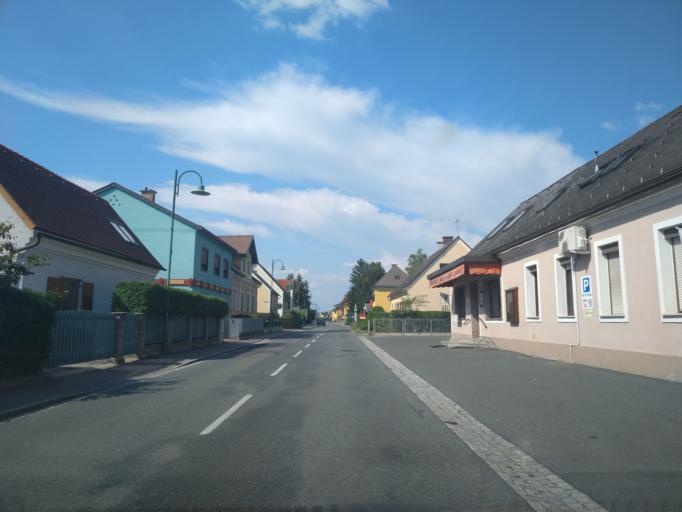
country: AT
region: Styria
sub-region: Politischer Bezirk Leibnitz
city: Kaindorf an der Sulm
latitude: 46.7910
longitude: 15.5383
